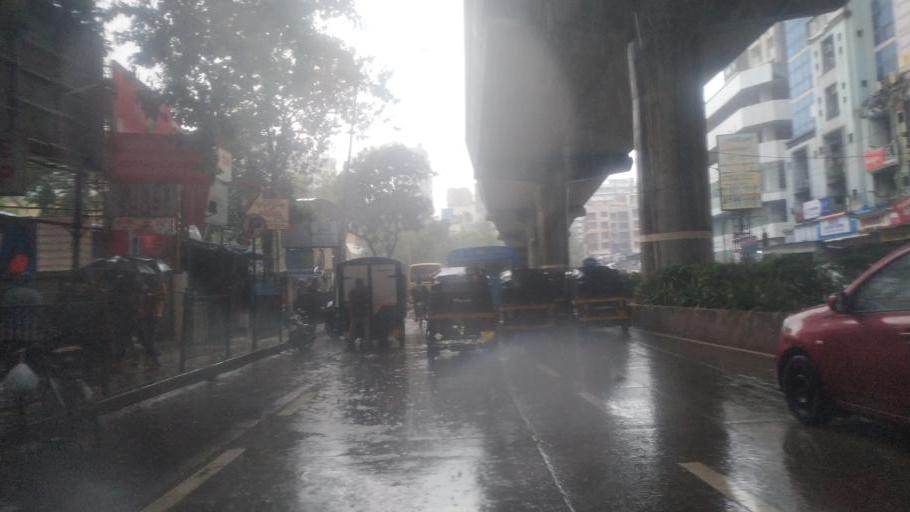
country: IN
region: Maharashtra
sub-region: Mumbai Suburban
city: Powai
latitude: 19.1272
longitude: 72.8354
